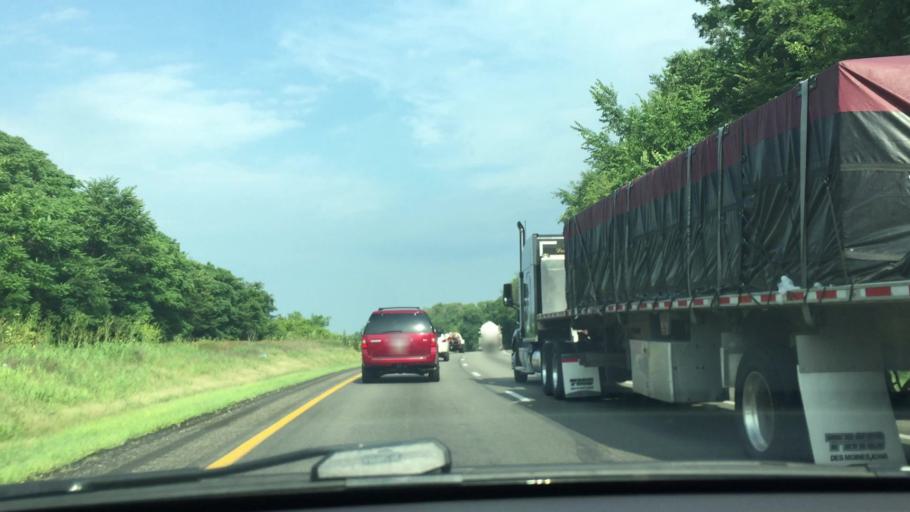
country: US
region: Pennsylvania
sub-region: Washington County
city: Wolfdale
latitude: 40.1310
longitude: -80.3515
